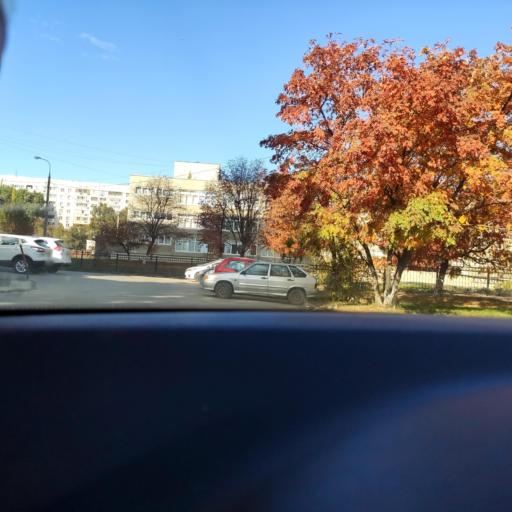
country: RU
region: Samara
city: Petra-Dubrava
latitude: 53.2304
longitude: 50.2694
